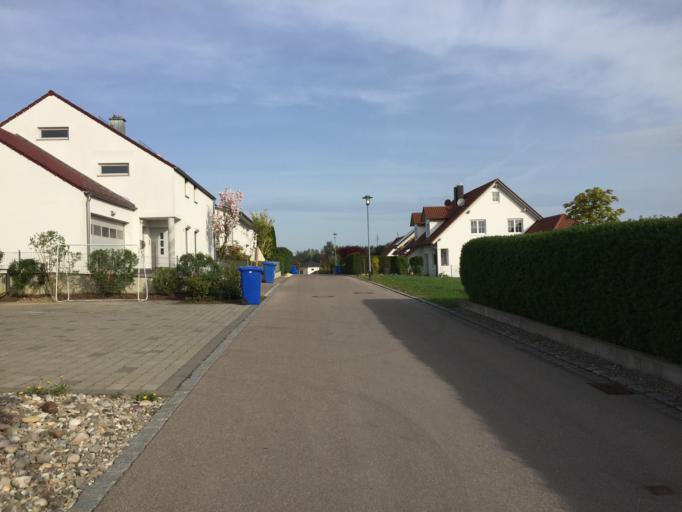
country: DE
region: Bavaria
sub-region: Swabia
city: Wertingen
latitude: 48.5679
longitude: 10.6778
